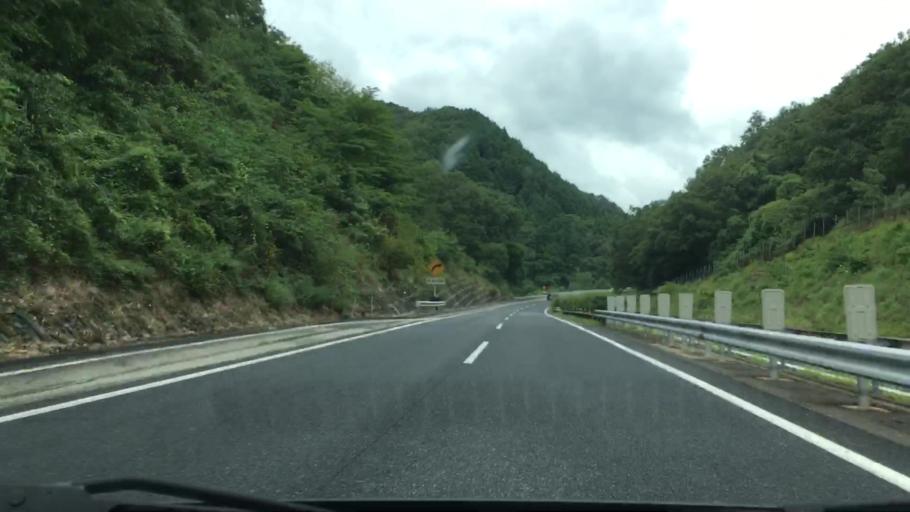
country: JP
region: Okayama
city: Tsuyama
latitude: 35.0197
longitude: 134.2080
